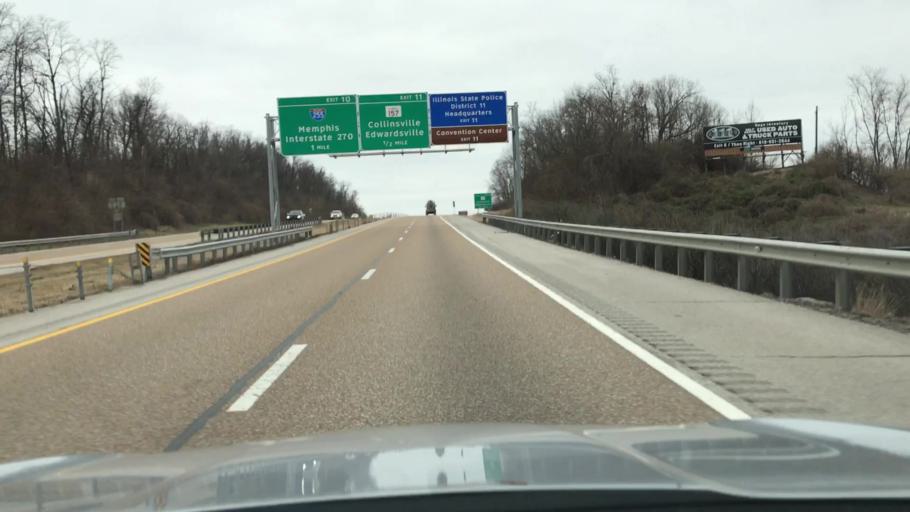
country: US
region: Illinois
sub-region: Madison County
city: Collinsville
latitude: 38.6856
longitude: -90.0067
